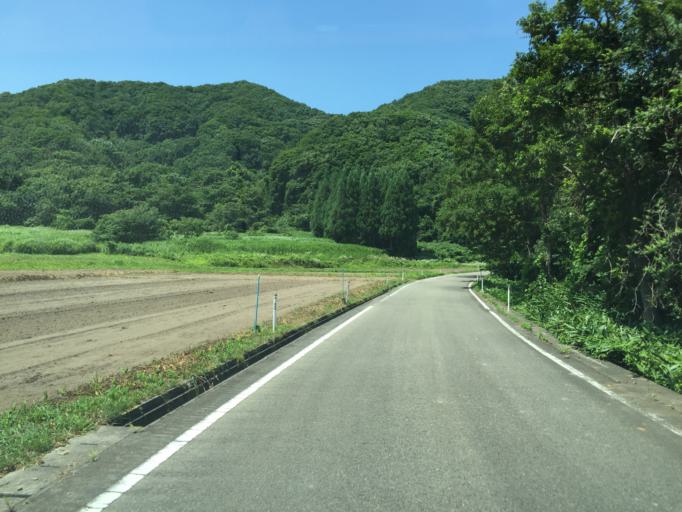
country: JP
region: Fukushima
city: Inawashiro
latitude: 37.4920
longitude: 140.0272
